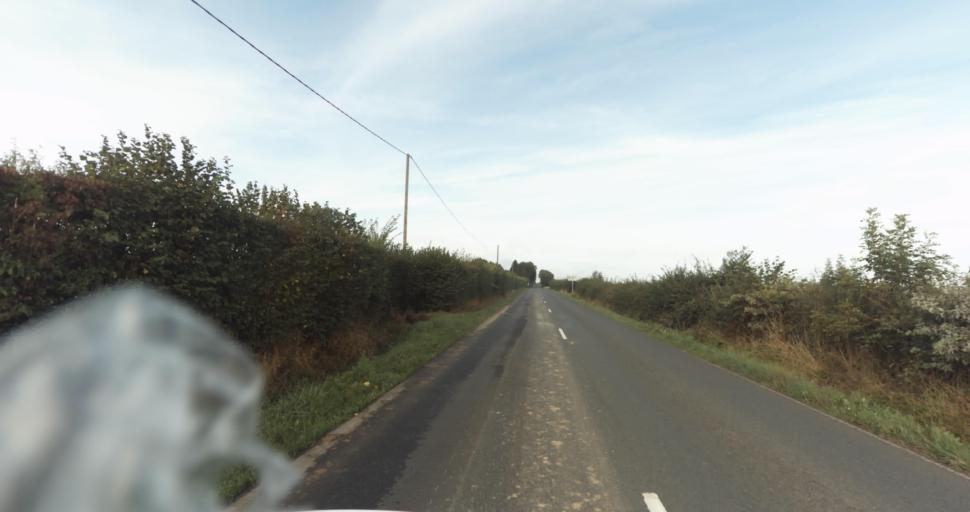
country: FR
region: Lower Normandy
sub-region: Departement de l'Orne
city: Gace
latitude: 48.8963
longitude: 0.3260
